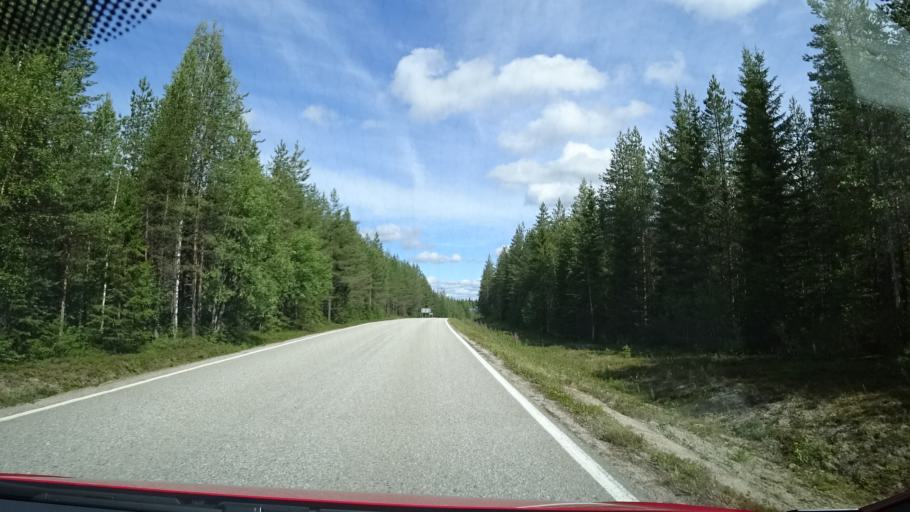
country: FI
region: Kainuu
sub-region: Kehys-Kainuu
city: Kuhmo
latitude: 64.5642
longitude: 29.6989
